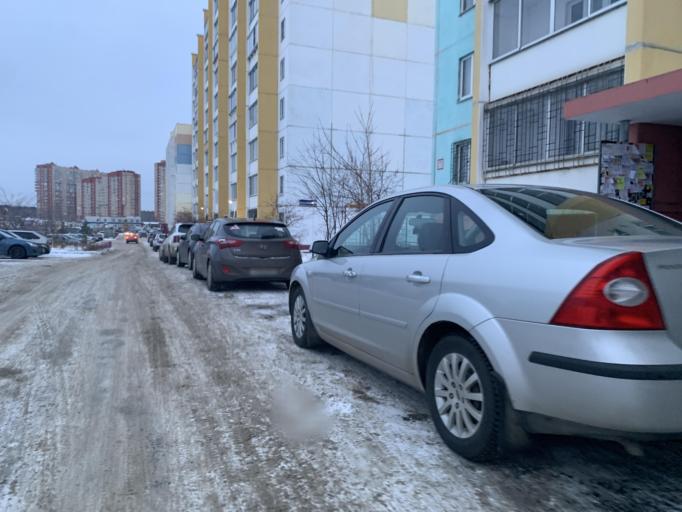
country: RU
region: Chelyabinsk
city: Roshchino
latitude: 55.1910
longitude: 61.2735
